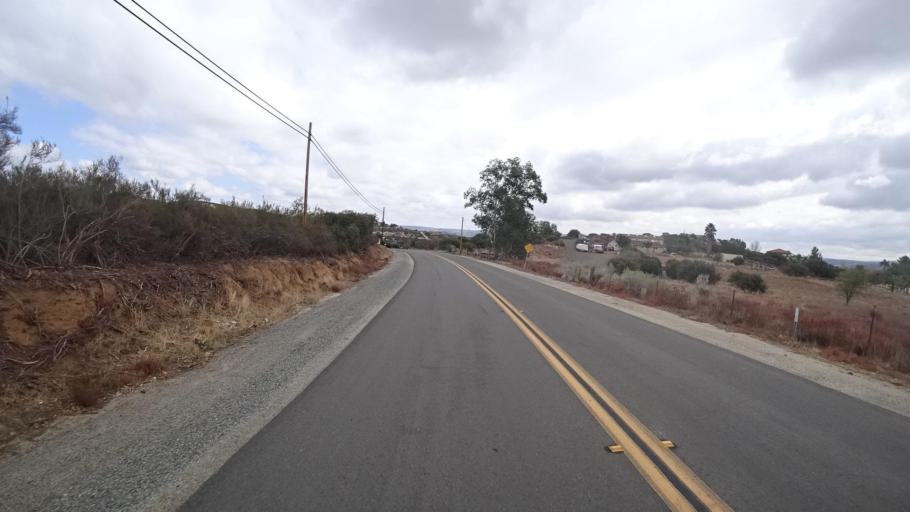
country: US
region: California
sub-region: San Diego County
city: Campo
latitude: 32.6478
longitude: -116.4934
